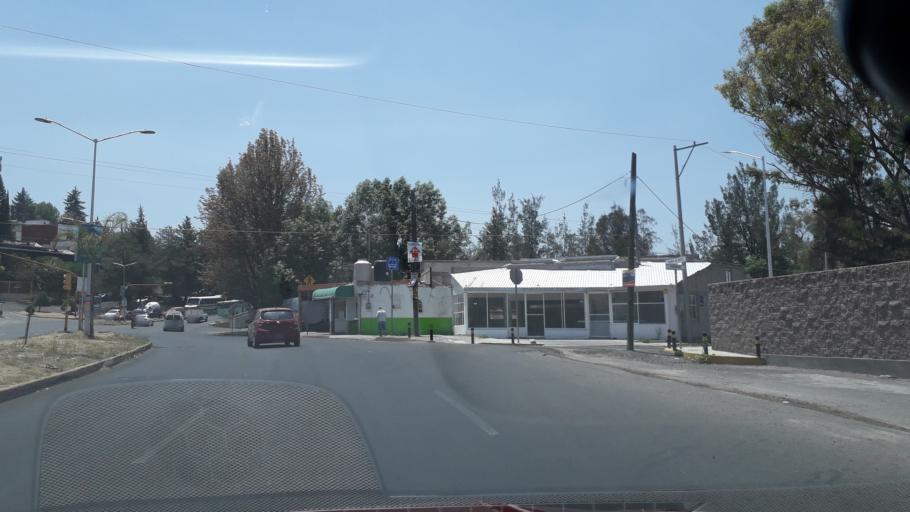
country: MX
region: Puebla
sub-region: Puebla
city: Galaxia la Calera
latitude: 19.0071
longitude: -98.1802
